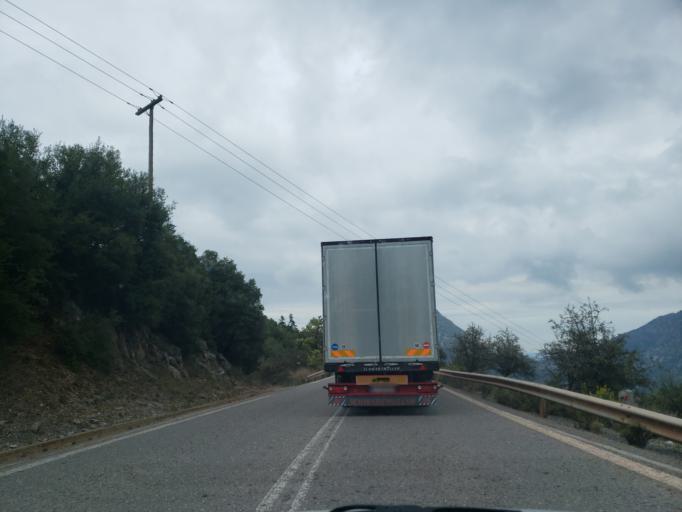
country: GR
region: Central Greece
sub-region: Nomos Fokidos
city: Amfissa
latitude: 38.6406
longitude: 22.3954
